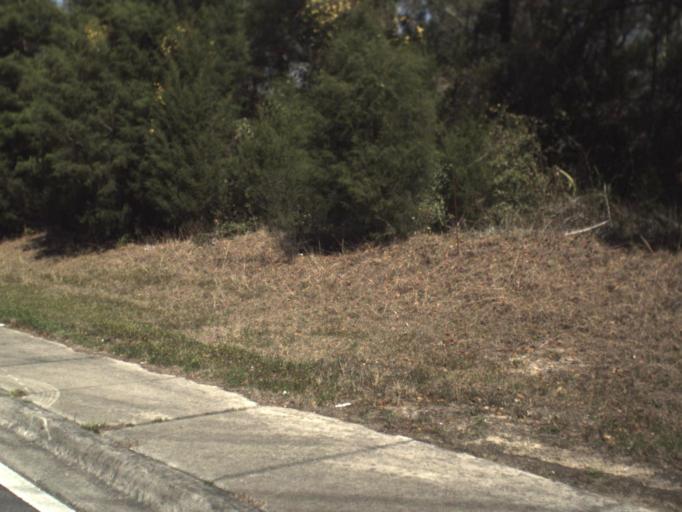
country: US
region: Florida
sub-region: Jackson County
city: Marianna
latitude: 30.7521
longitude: -85.1922
